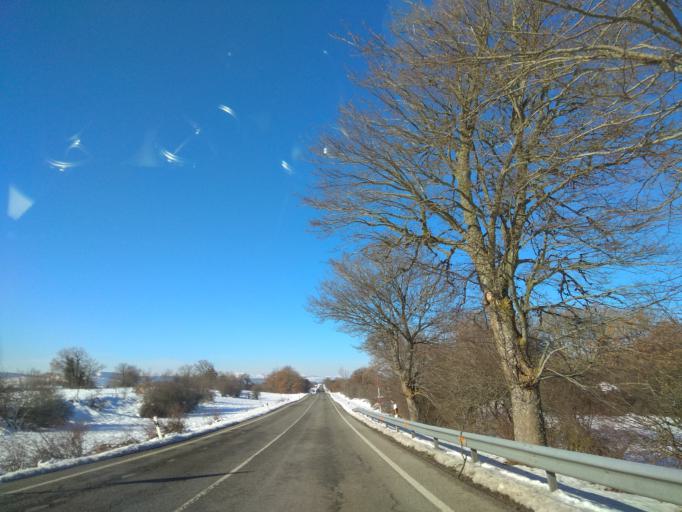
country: ES
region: Cantabria
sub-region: Provincia de Cantabria
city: San Martin de Elines
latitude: 42.9385
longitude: -3.7308
